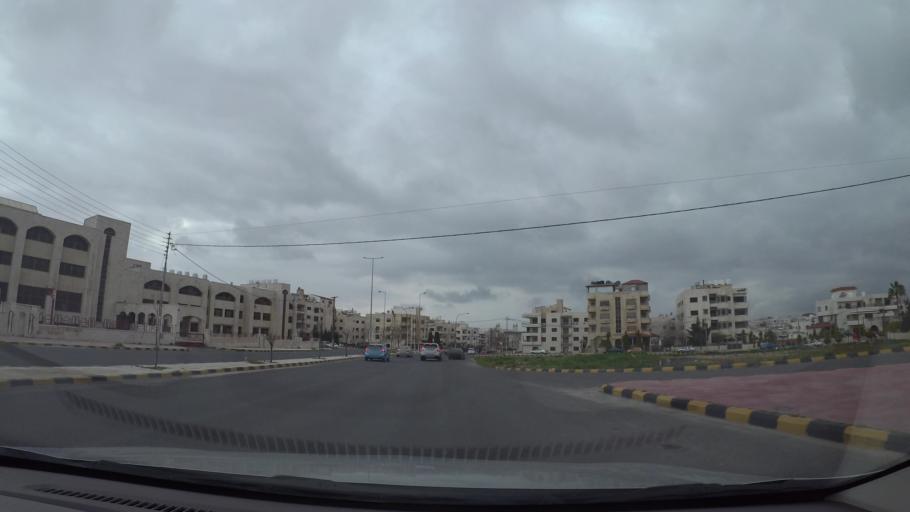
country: JO
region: Amman
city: Al Jubayhah
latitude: 31.9892
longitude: 35.8417
